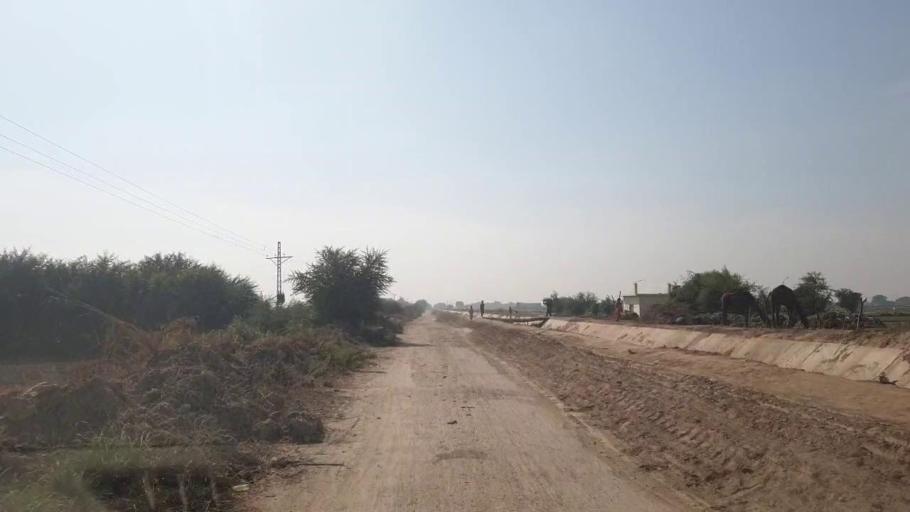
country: PK
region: Sindh
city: Matiari
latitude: 25.6690
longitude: 68.3473
